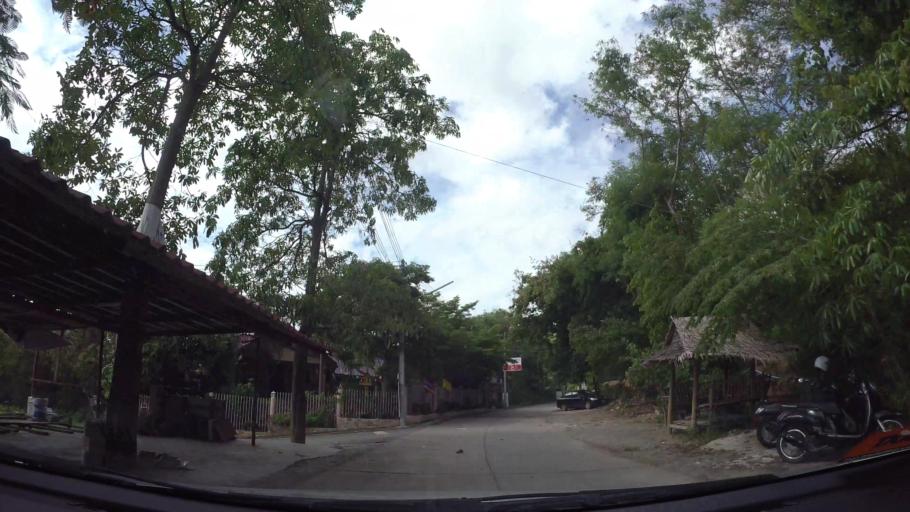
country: TH
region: Chon Buri
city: Sattahip
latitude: 12.6961
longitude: 100.9043
